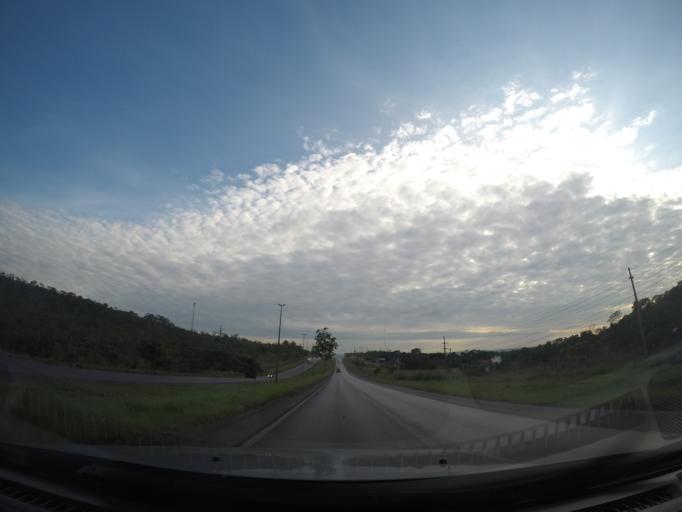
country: BR
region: Goias
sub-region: Planaltina
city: Planaltina
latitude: -15.6222
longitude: -47.7184
